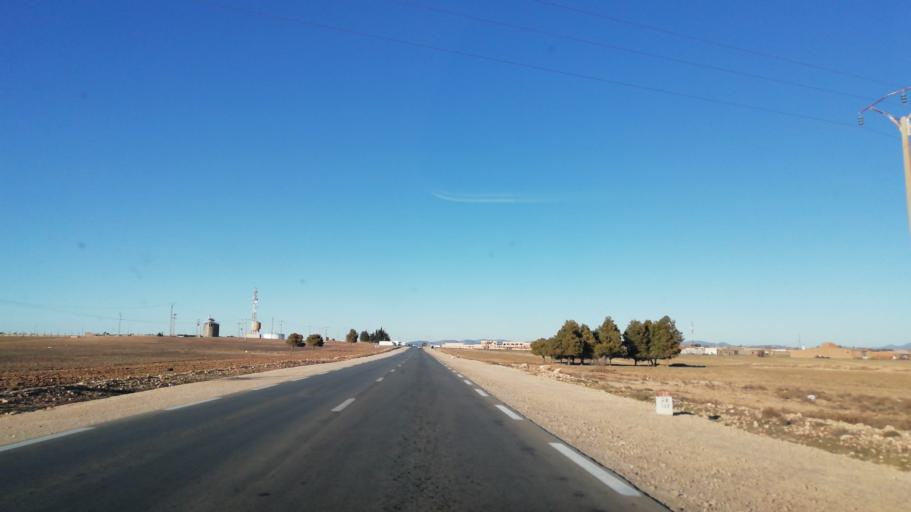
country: DZ
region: Tlemcen
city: Sebdou
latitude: 34.4747
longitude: -1.2715
